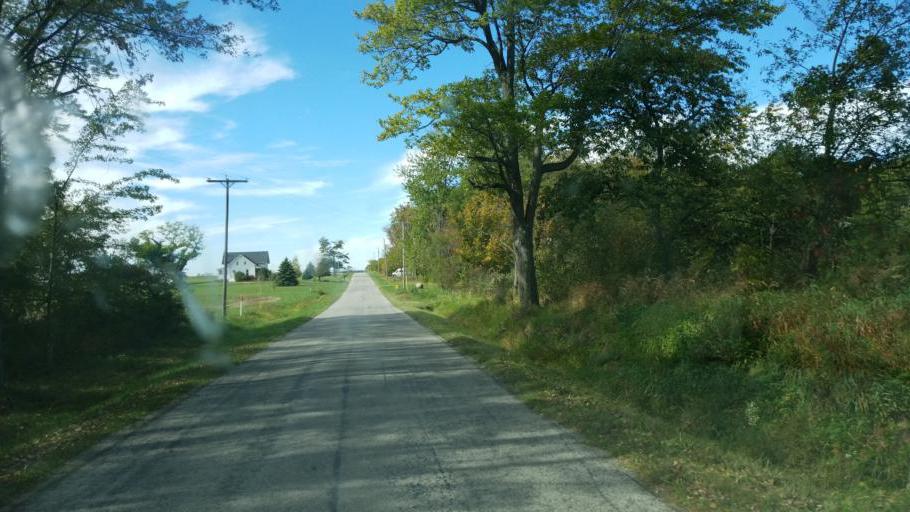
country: US
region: Ohio
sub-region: Huron County
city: Wakeman
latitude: 41.2845
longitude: -82.4722
